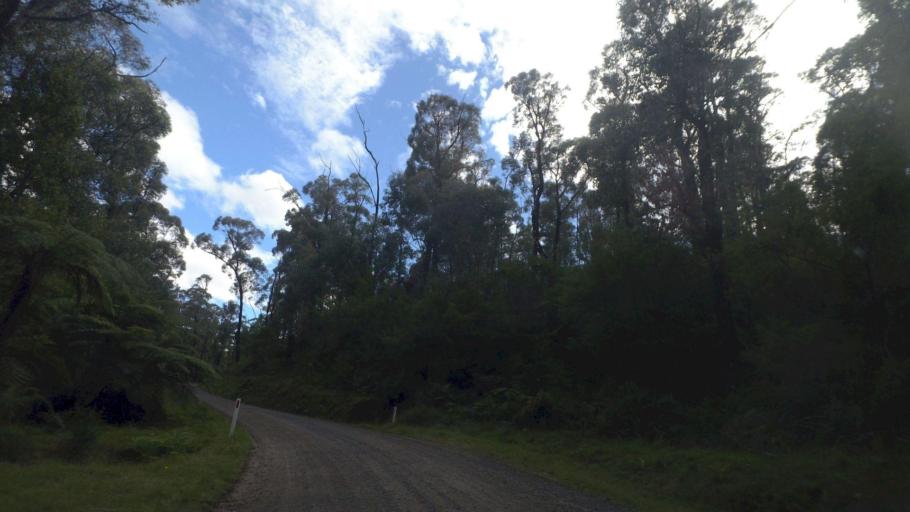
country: AU
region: Victoria
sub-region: Cardinia
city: Bunyip
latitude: -37.9960
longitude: 145.8151
